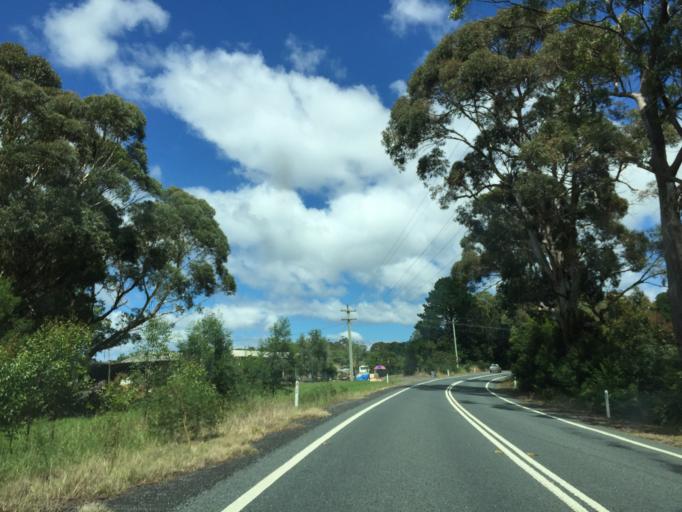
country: AU
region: New South Wales
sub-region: Blue Mountains Municipality
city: Lawson
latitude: -33.5279
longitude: 150.4569
